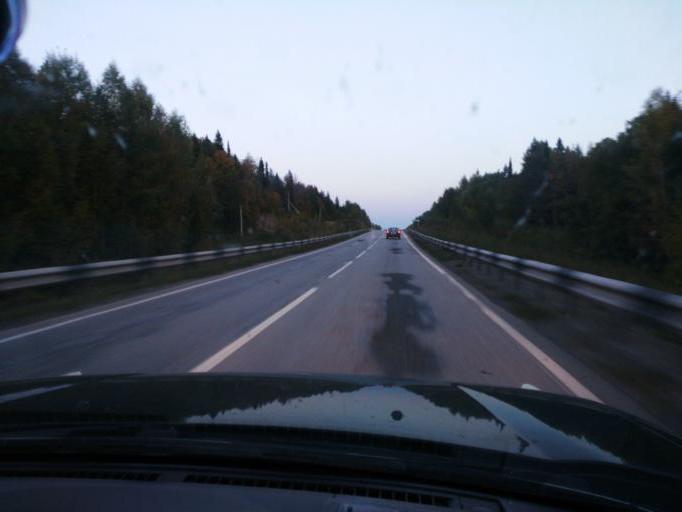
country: RU
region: Perm
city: Verkhnechusovskiye Gorodki
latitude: 58.2718
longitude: 56.9466
